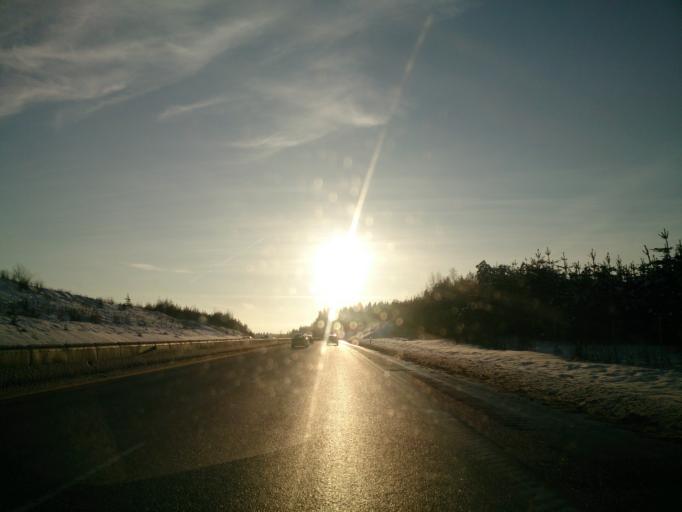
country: SE
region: OEstergoetland
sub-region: Norrkopings Kommun
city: Kimstad
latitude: 58.5657
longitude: 16.0693
